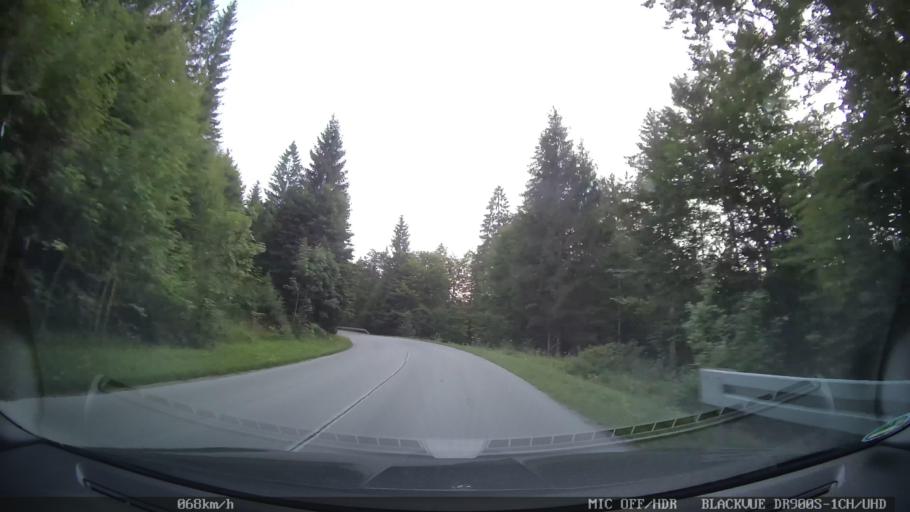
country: HR
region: Karlovacka
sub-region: Grad Ogulin
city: Ogulin
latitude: 45.2394
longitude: 15.1376
